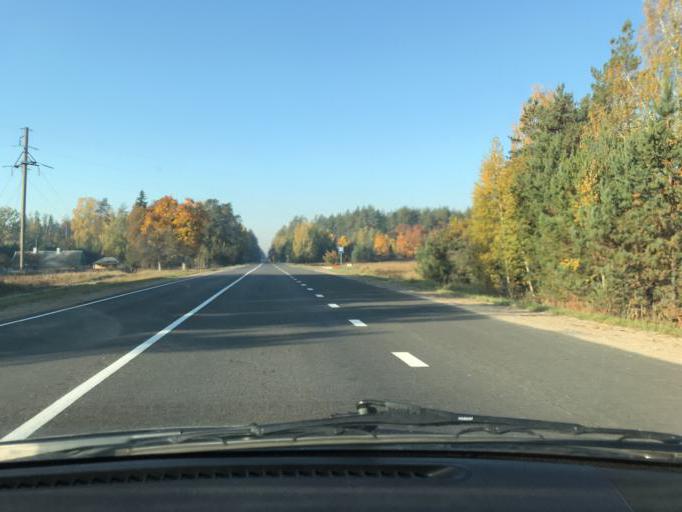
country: BY
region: Brest
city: Tsyelyakhany
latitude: 52.8755
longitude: 25.7422
